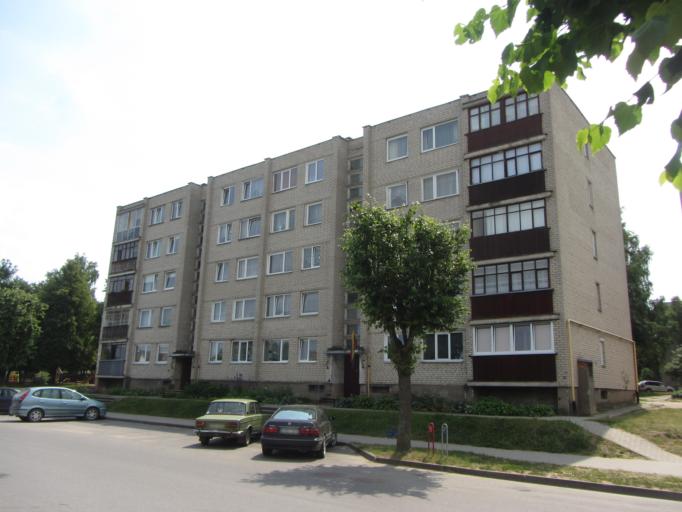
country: LT
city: Zarasai
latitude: 55.7351
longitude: 26.2452
